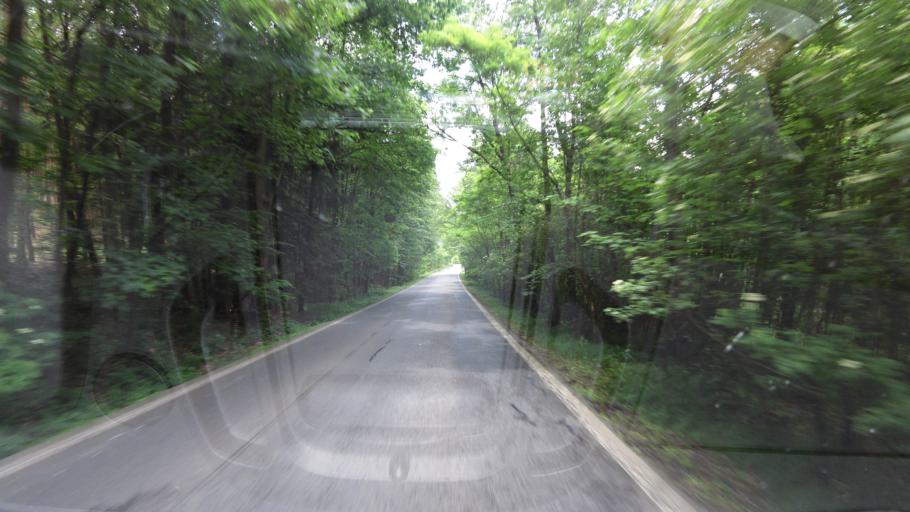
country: CZ
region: Plzensky
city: St'ahlavy
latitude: 49.6848
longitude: 13.5117
